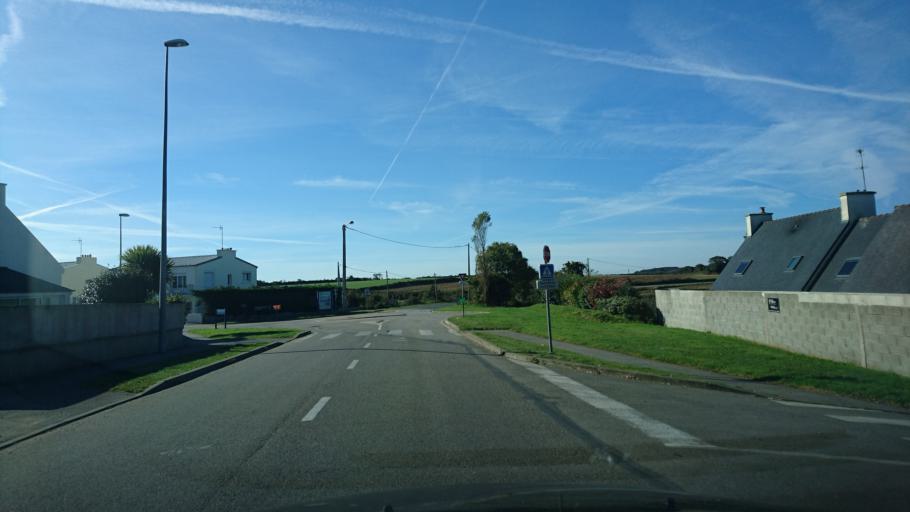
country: FR
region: Brittany
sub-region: Departement du Finistere
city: Saint-Renan
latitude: 48.4309
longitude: -4.6327
